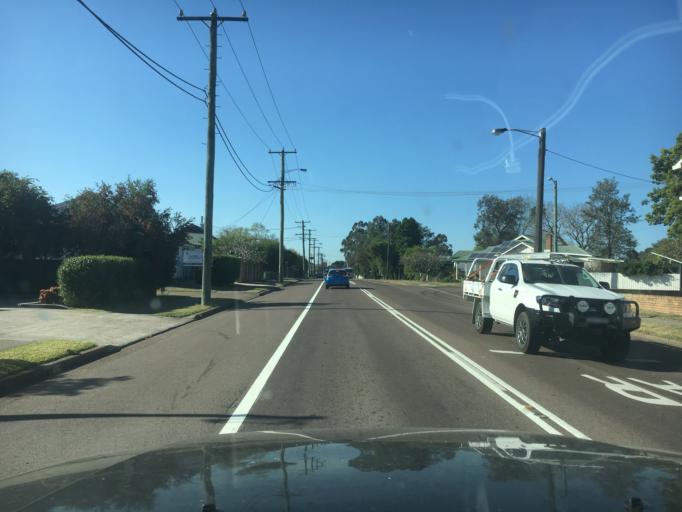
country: AU
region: New South Wales
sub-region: Singleton
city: Singleton
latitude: -32.5658
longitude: 151.1779
